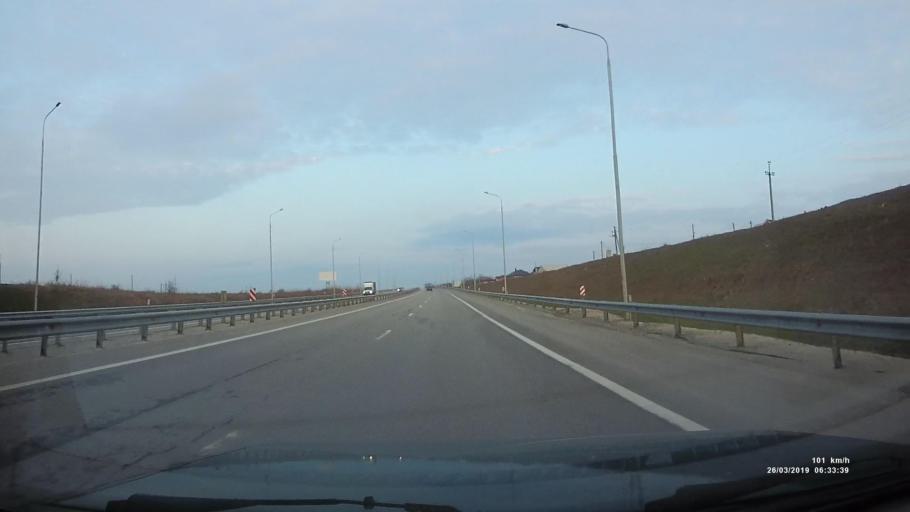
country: RU
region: Rostov
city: Chaltyr
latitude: 47.2723
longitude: 39.4865
